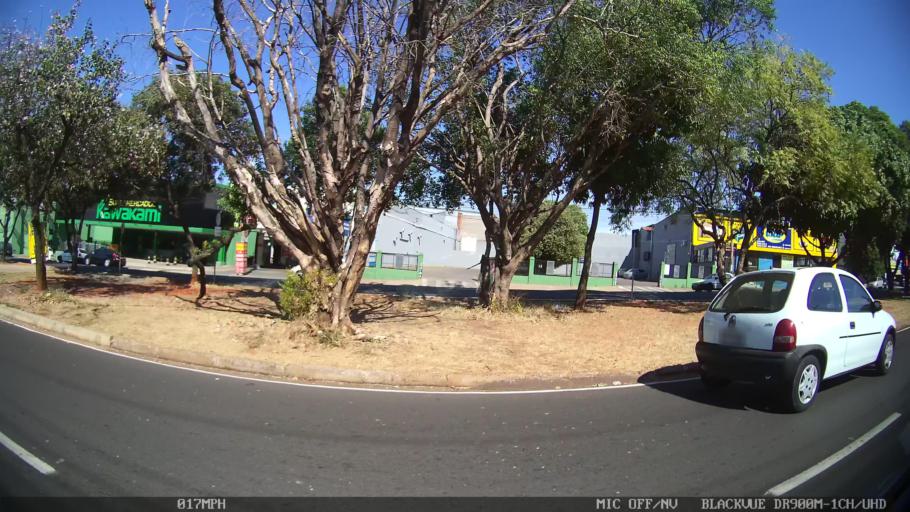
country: BR
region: Sao Paulo
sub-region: Sao Jose Do Rio Preto
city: Sao Jose do Rio Preto
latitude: -20.7779
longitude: -49.4042
